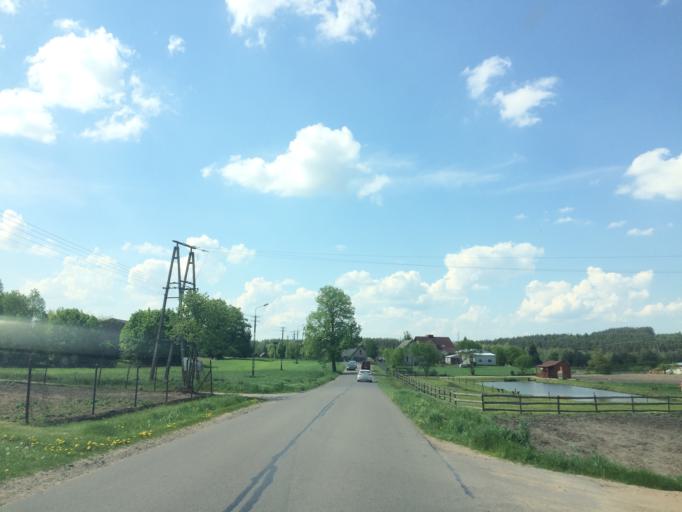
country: PL
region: Warmian-Masurian Voivodeship
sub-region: Powiat ilawski
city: Lubawa
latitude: 53.4320
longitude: 19.6958
